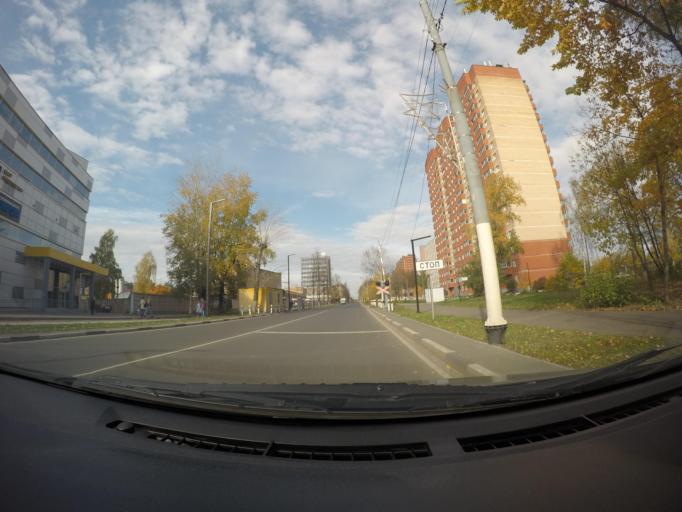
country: RU
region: Moscow
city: Severnyy
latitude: 55.9265
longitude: 37.5233
